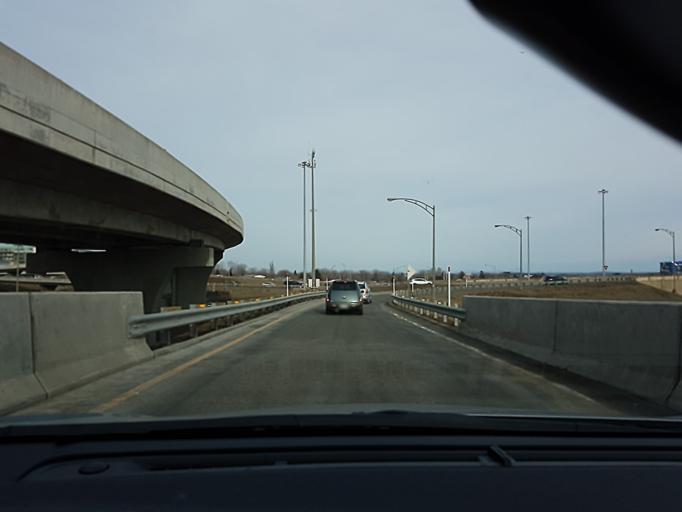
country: CA
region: Quebec
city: L'Ancienne-Lorette
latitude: 46.7612
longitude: -71.3006
